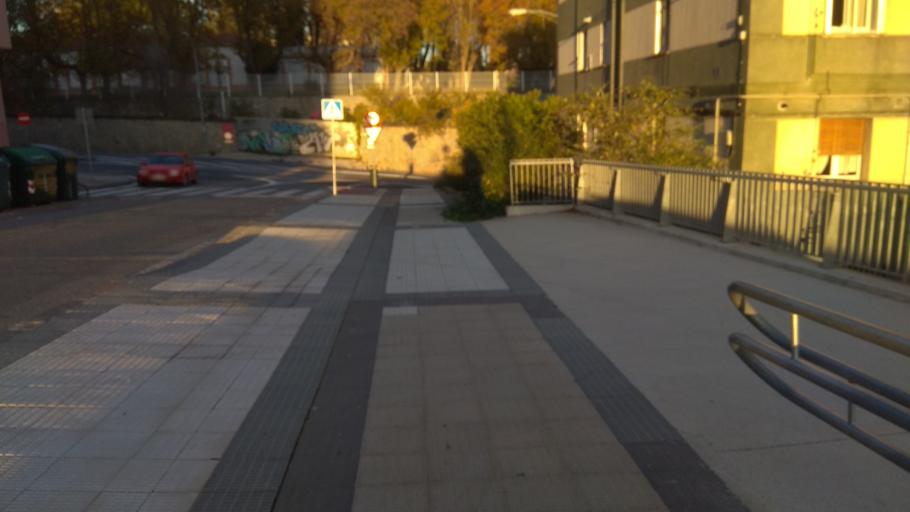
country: ES
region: Navarre
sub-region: Provincia de Navarra
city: Baranain
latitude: 42.8025
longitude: -1.6703
